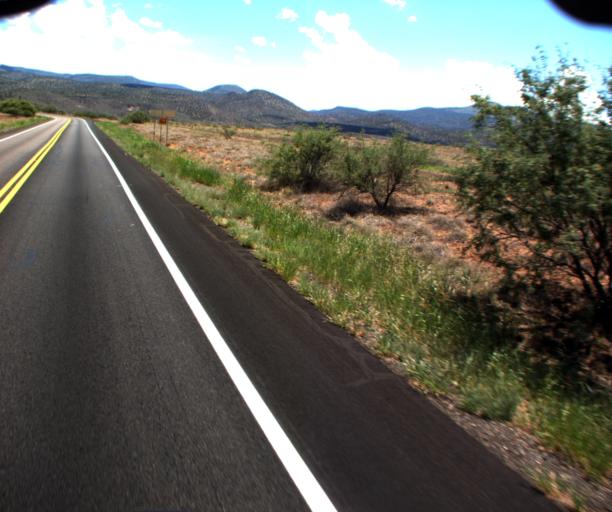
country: US
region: Arizona
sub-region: Yavapai County
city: Camp Verde
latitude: 34.5068
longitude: -111.7645
